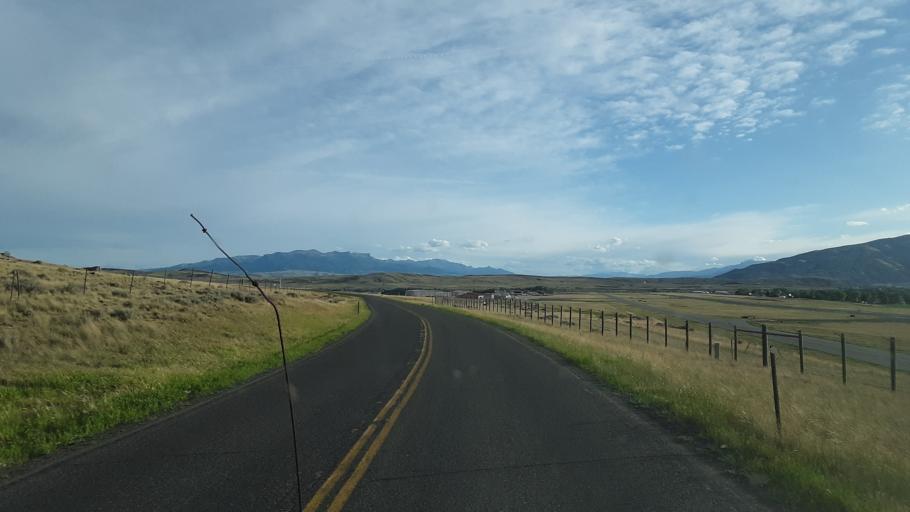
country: US
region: Wyoming
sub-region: Park County
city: Cody
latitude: 44.5239
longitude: -109.0133
